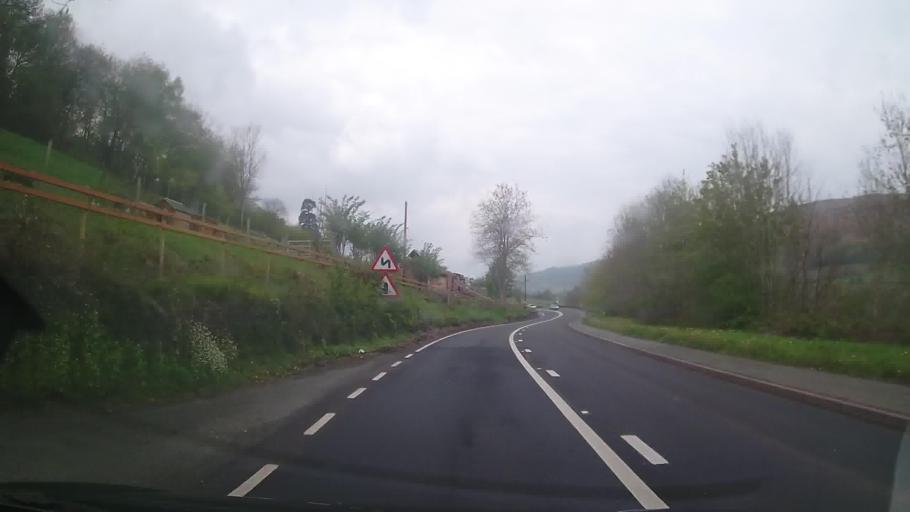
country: GB
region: Wales
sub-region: Denbighshire
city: Bryneglwys
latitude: 52.9746
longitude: -3.2773
